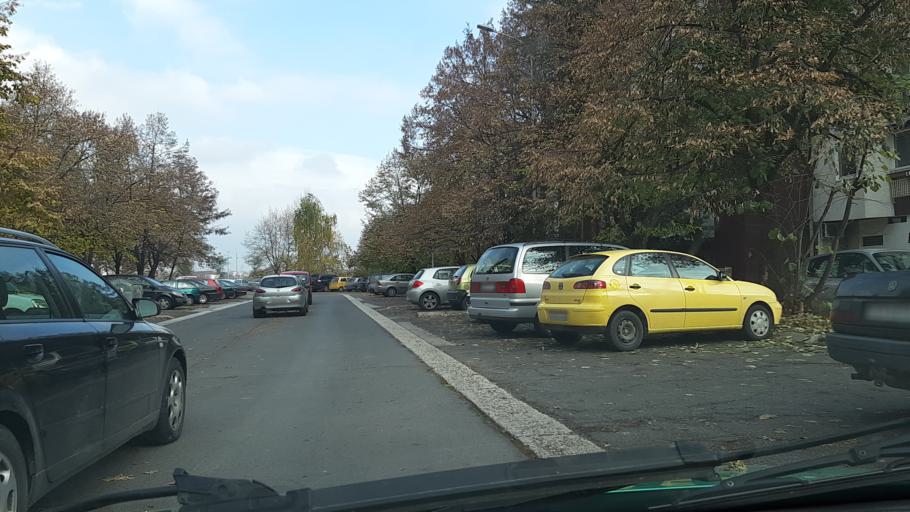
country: MK
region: Kisela Voda
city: Usje
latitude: 41.9901
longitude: 21.4686
